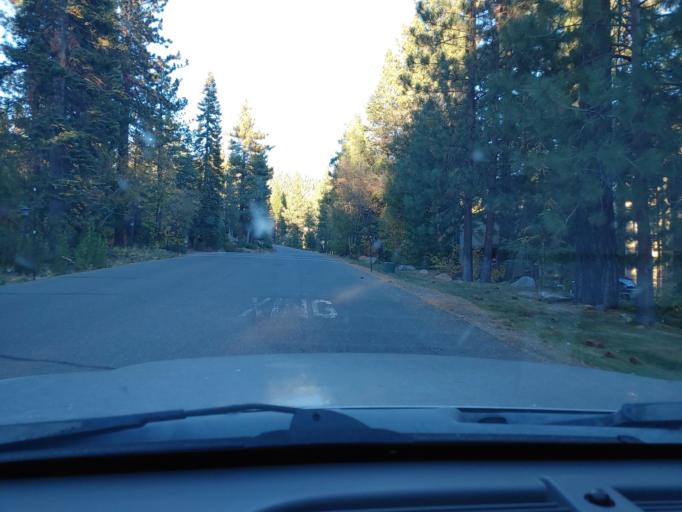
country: US
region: California
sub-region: Placer County
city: Kings Beach
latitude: 39.2513
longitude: -120.0340
